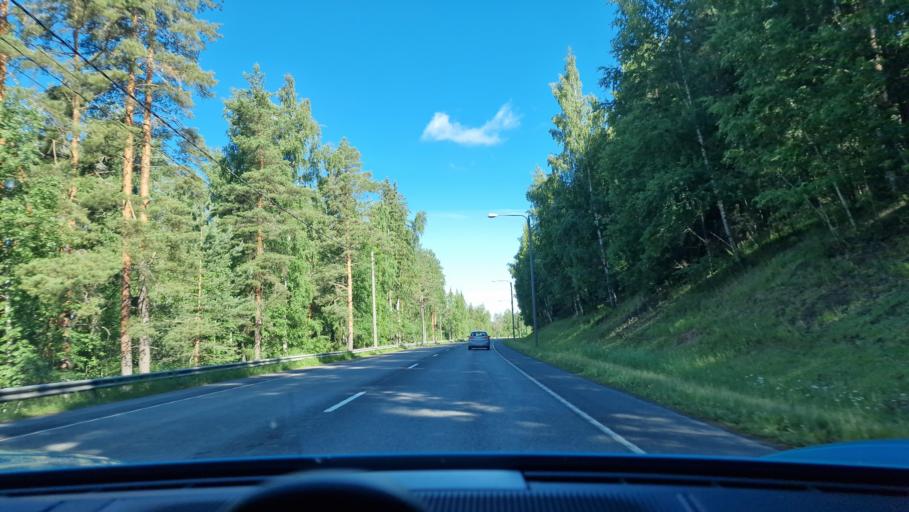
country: FI
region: Pirkanmaa
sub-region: Tampere
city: Kangasala
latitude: 61.4307
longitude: 24.1294
